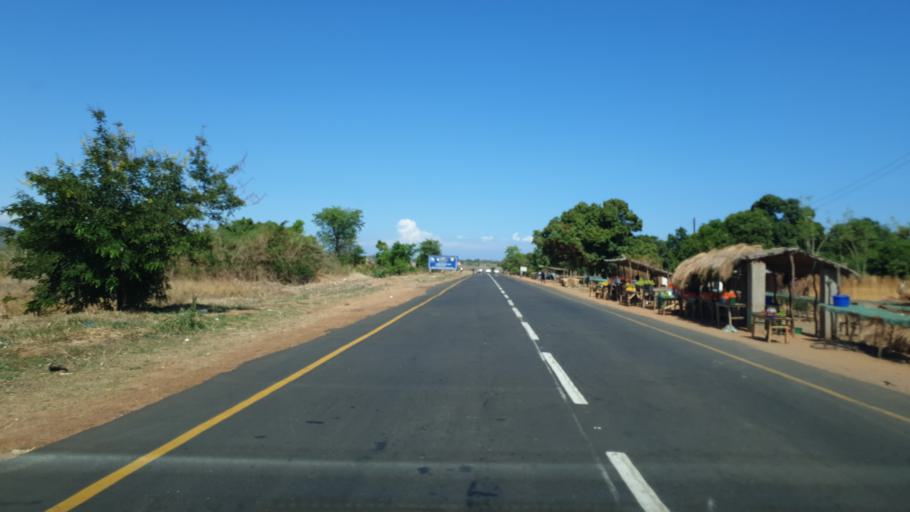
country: MW
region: Central Region
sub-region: Salima District
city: Salima
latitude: -13.7673
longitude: 34.5537
